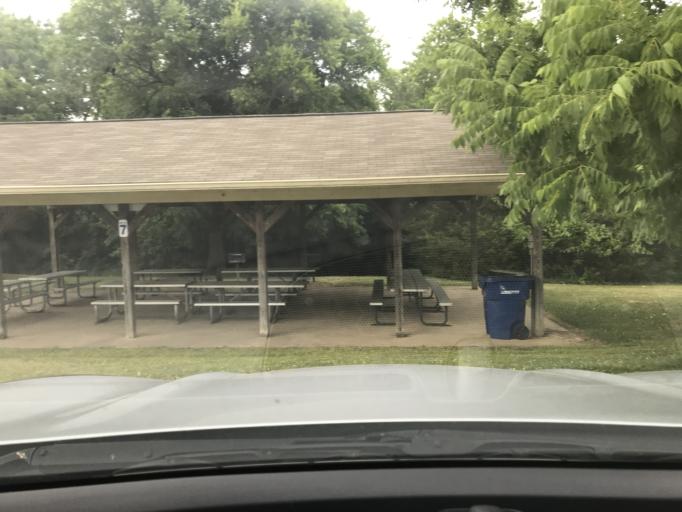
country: US
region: Tennessee
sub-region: Davidson County
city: Goodlettsville
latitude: 36.3055
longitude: -86.7083
